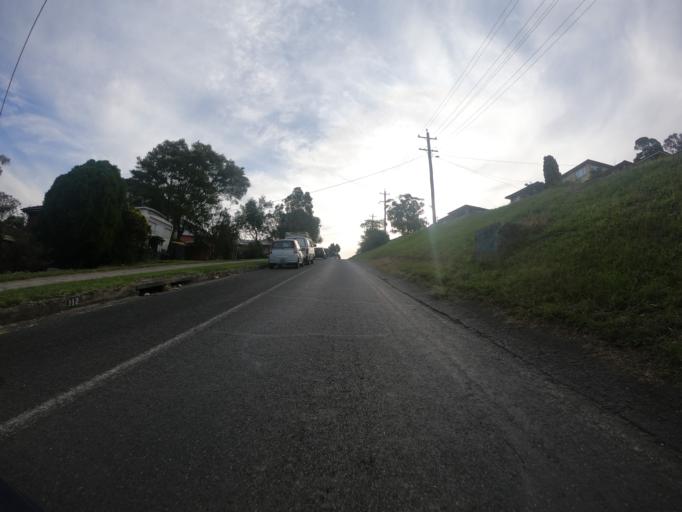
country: AU
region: New South Wales
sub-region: Wollongong
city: West Wollongong
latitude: -34.4352
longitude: 150.8540
